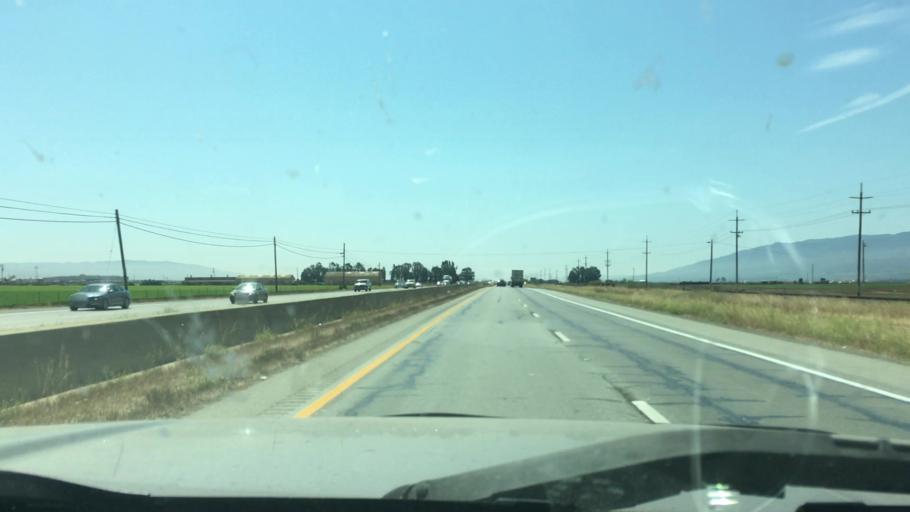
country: US
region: California
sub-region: Monterey County
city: Chualar
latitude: 36.6003
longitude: -121.5505
